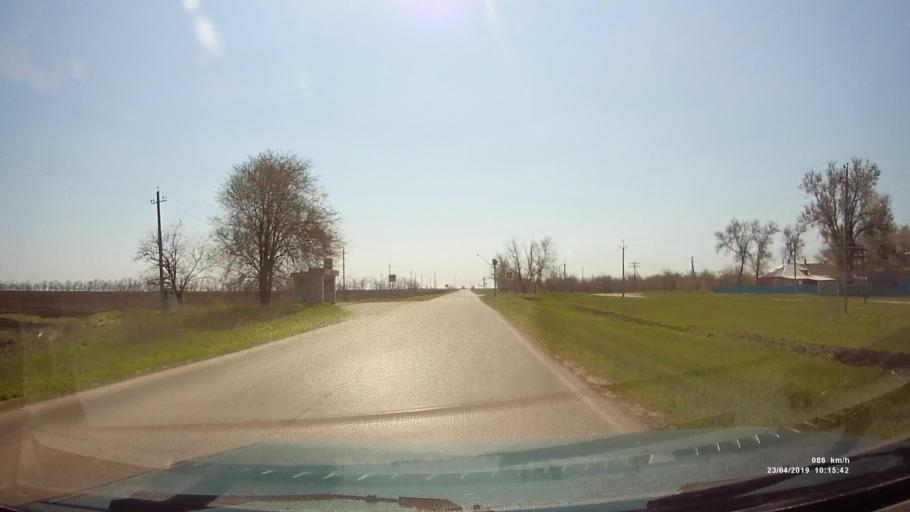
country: RU
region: Rostov
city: Sovetskoye
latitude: 46.6645
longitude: 42.3850
